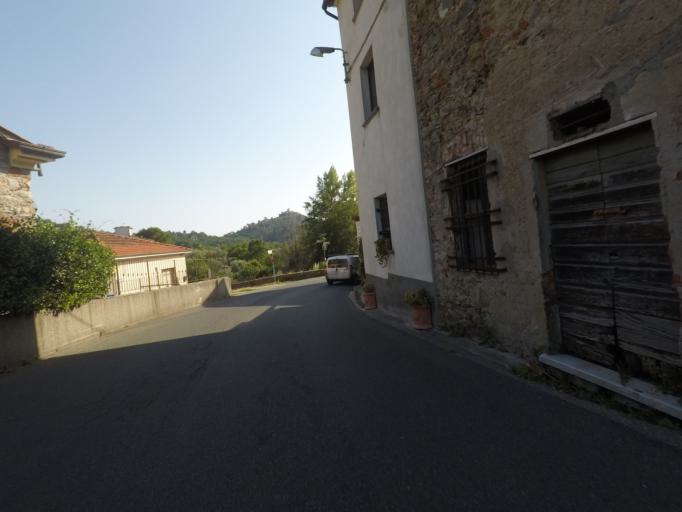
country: IT
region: Liguria
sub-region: Provincia di La Spezia
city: Casano-Dogana-Isola
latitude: 44.0890
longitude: 10.0459
